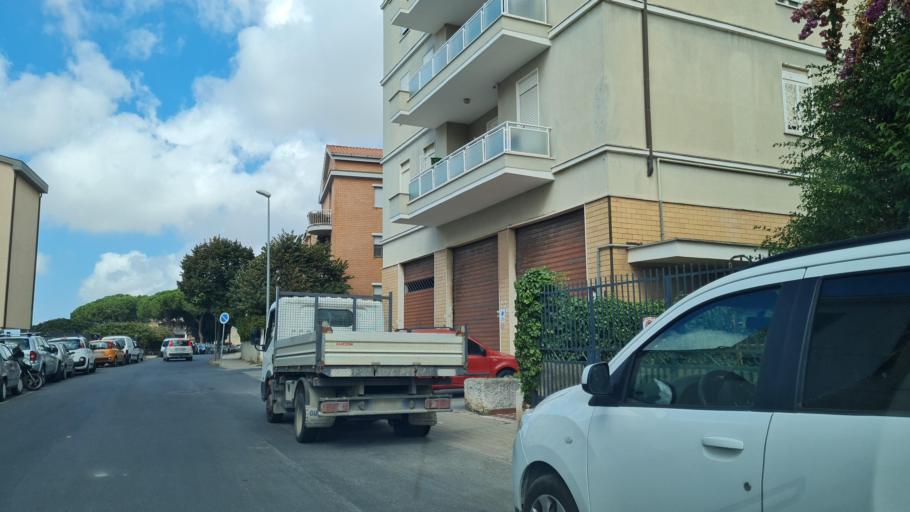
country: IT
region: Latium
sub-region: Provincia di Viterbo
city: Tarquinia
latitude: 42.2515
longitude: 11.7631
